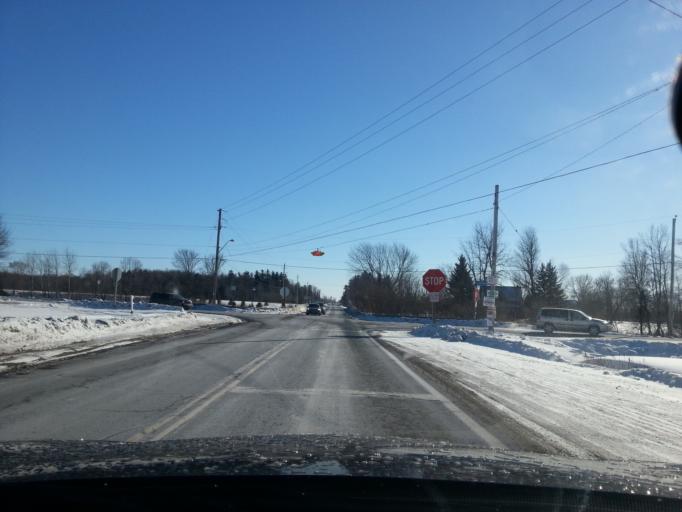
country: CA
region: Ontario
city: Bourget
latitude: 45.2557
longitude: -75.3971
